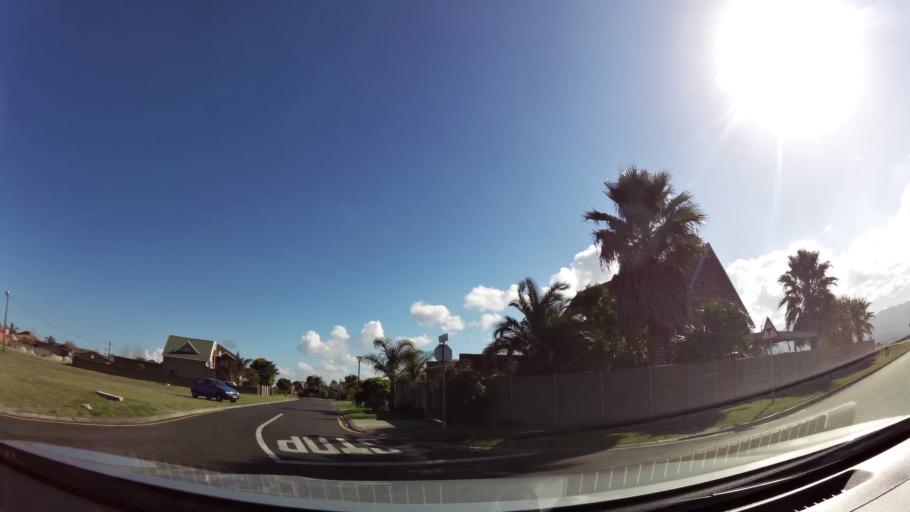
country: ZA
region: Western Cape
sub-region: Eden District Municipality
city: George
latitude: -33.9837
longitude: 22.4371
